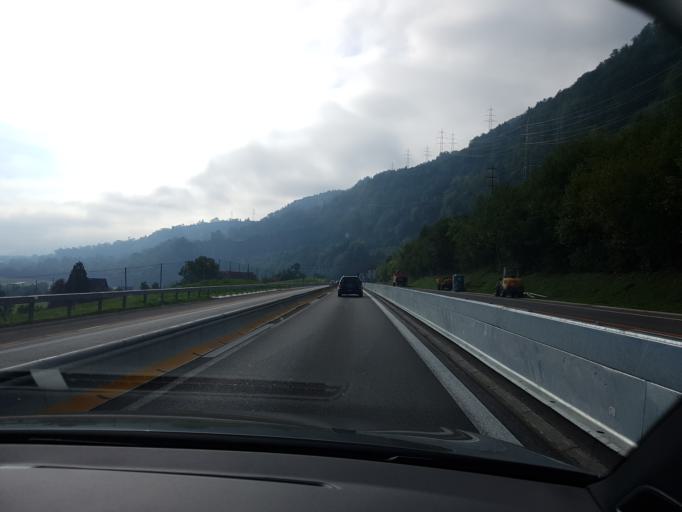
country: CH
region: Schwyz
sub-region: Bezirk Schwyz
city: Arth
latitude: 47.0593
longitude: 8.5129
